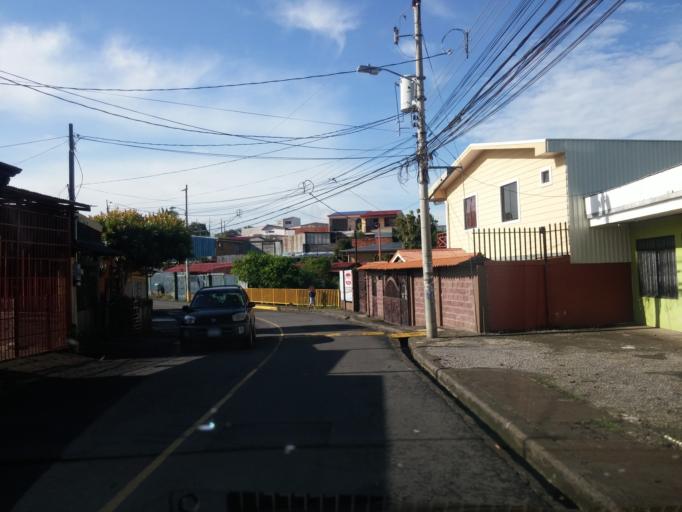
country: CR
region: Heredia
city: Mercedes
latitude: 10.0046
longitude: -84.1385
